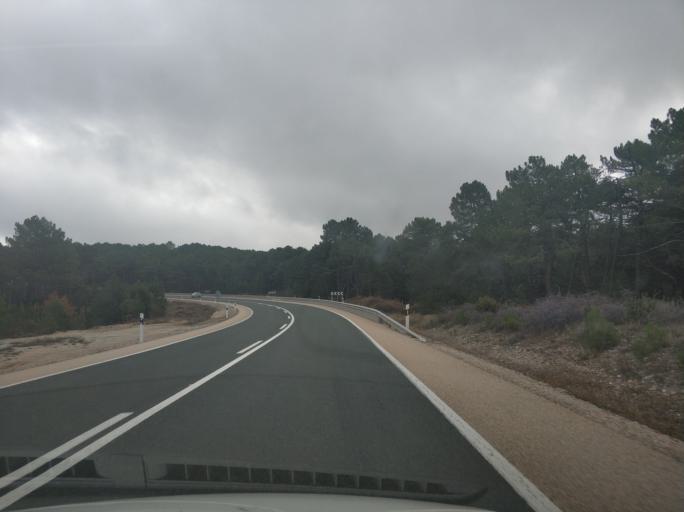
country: ES
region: Castille and Leon
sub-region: Provincia de Soria
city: Muriel Viejo
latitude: 41.8183
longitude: -2.9343
